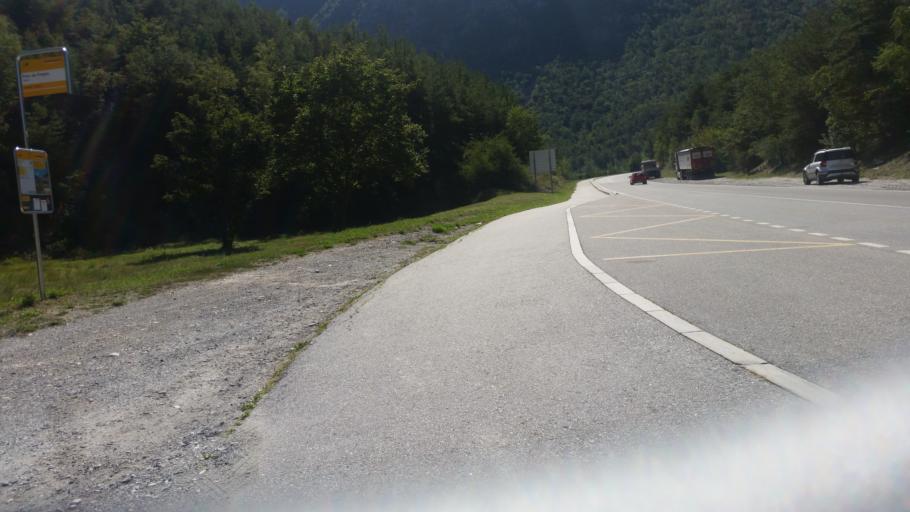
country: CH
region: Valais
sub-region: Sierre District
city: Chippis
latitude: 46.2928
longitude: 7.5585
